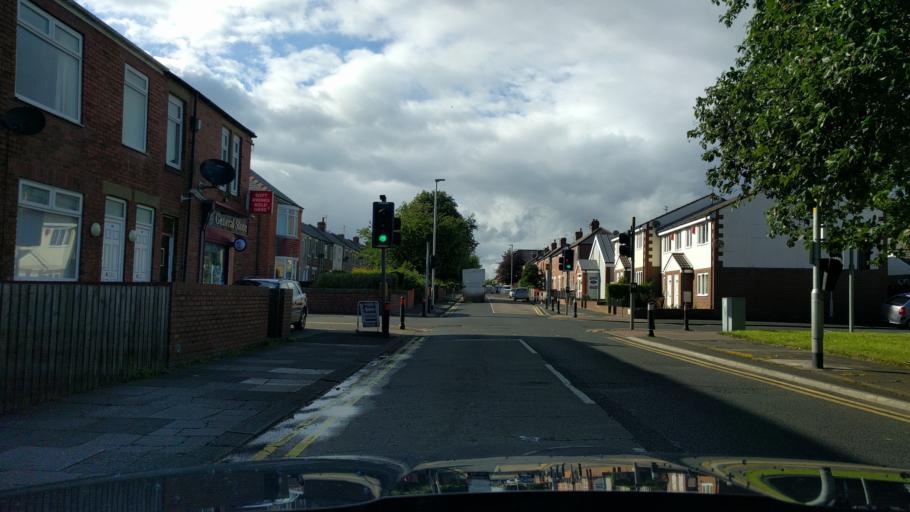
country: GB
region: England
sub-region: Northumberland
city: Ashington
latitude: 55.1755
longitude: -1.5581
